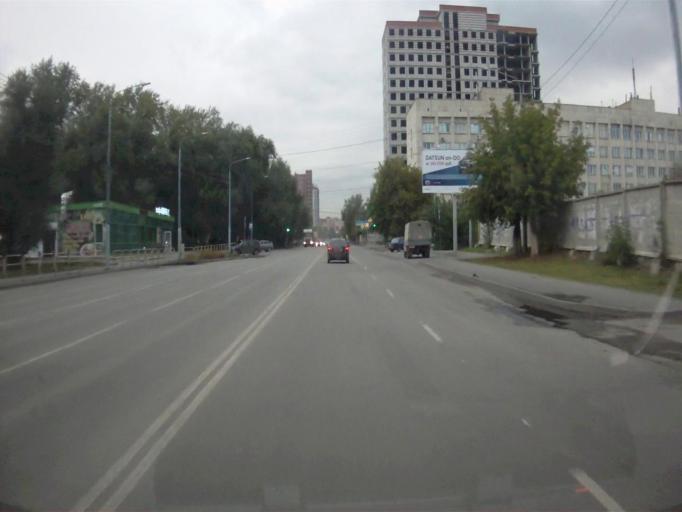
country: RU
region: Chelyabinsk
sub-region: Gorod Chelyabinsk
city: Chelyabinsk
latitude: 55.1466
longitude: 61.3986
